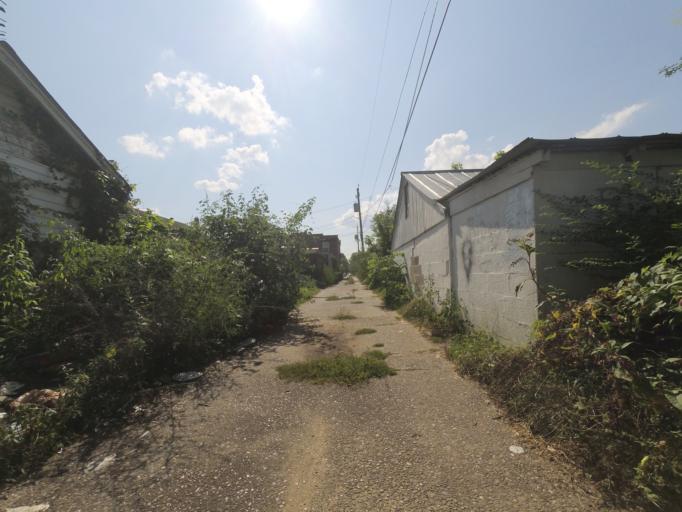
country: US
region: West Virginia
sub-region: Cabell County
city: Huntington
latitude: 38.4148
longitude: -82.4621
